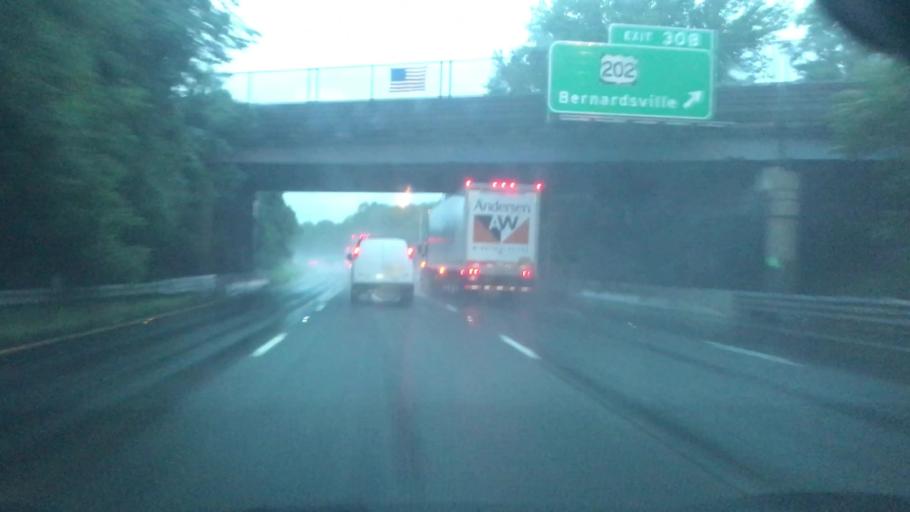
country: US
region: New Jersey
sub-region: Somerset County
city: Bernardsville
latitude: 40.7286
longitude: -74.5391
